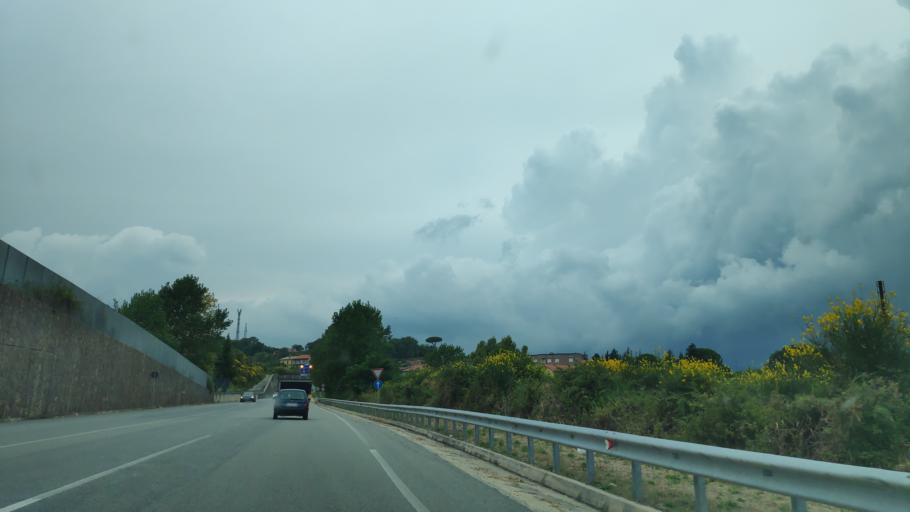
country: IT
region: Calabria
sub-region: Provincia di Catanzaro
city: Argusto
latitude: 38.6803
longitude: 16.4243
